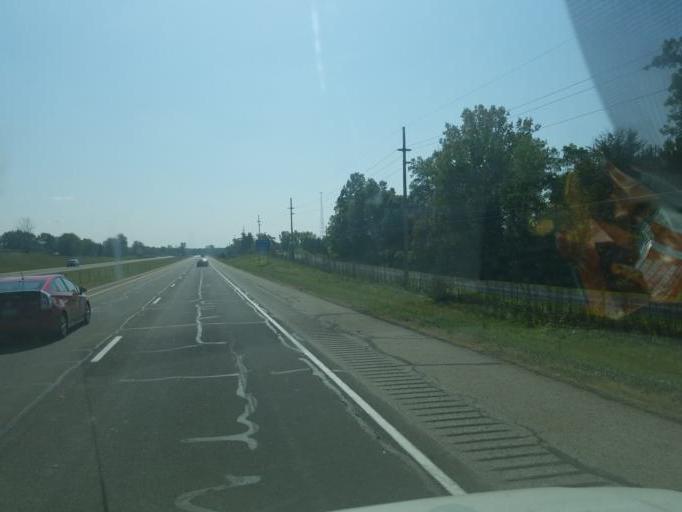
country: US
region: Indiana
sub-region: Steuben County
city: Angola
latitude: 41.6136
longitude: -85.0477
